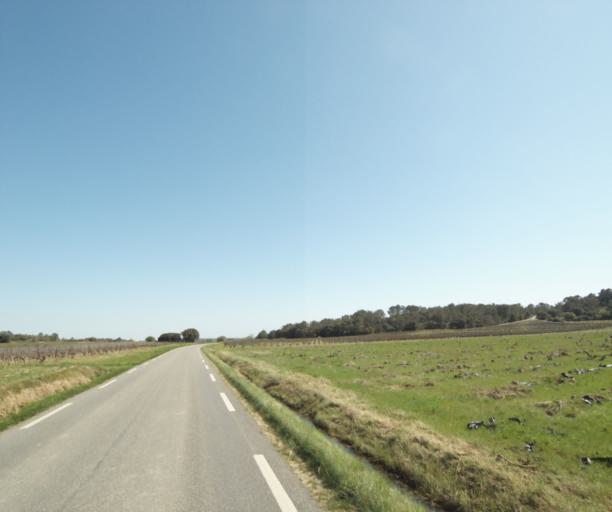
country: FR
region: Languedoc-Roussillon
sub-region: Departement de l'Herault
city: Saint-Drezery
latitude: 43.7464
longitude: 3.9671
